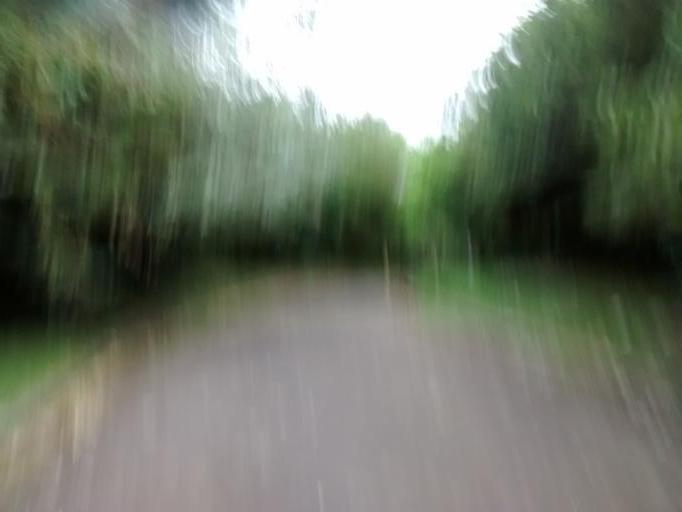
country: FR
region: Brittany
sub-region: Departement d'Ille-et-Vilaine
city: Cesson-Sevigne
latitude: 48.1265
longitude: -1.6202
